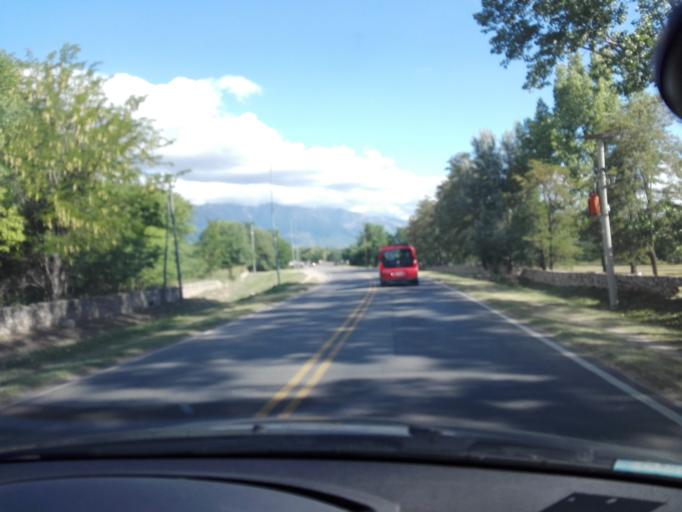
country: AR
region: Cordoba
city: Mina Clavero
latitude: -31.8031
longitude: -65.0052
